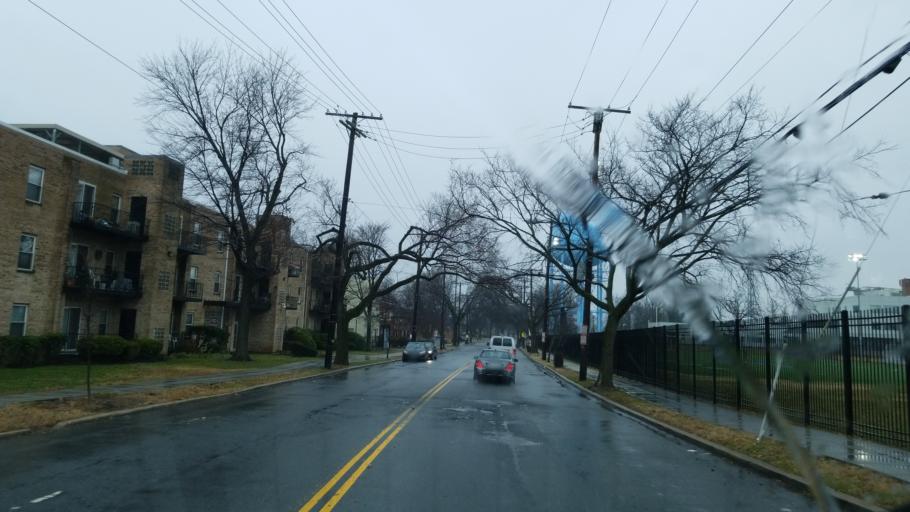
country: US
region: Maryland
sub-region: Prince George's County
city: Hillcrest Heights
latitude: 38.8574
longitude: -76.9700
